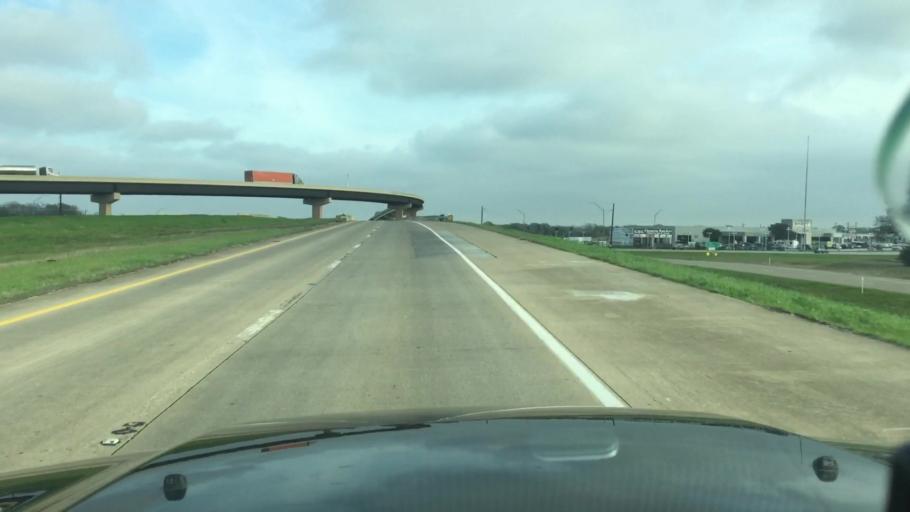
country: US
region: Texas
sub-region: Waller County
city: Hempstead
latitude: 30.1145
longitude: -96.0775
